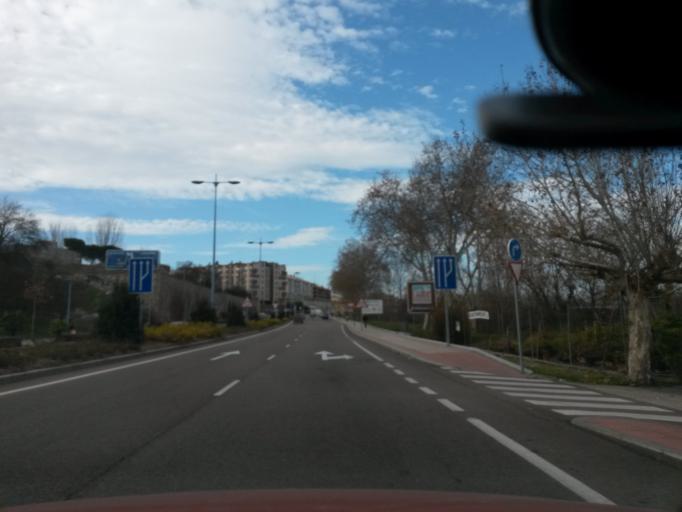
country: ES
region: Castille and Leon
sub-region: Provincia de Salamanca
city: Salamanca
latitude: 40.9523
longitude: -5.6584
